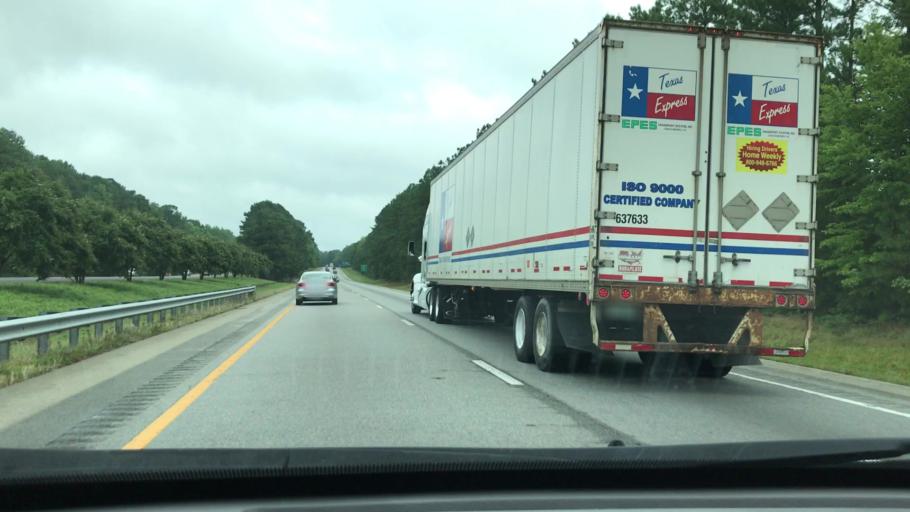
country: US
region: North Carolina
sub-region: Northampton County
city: Gaston
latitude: 36.5091
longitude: -77.5924
